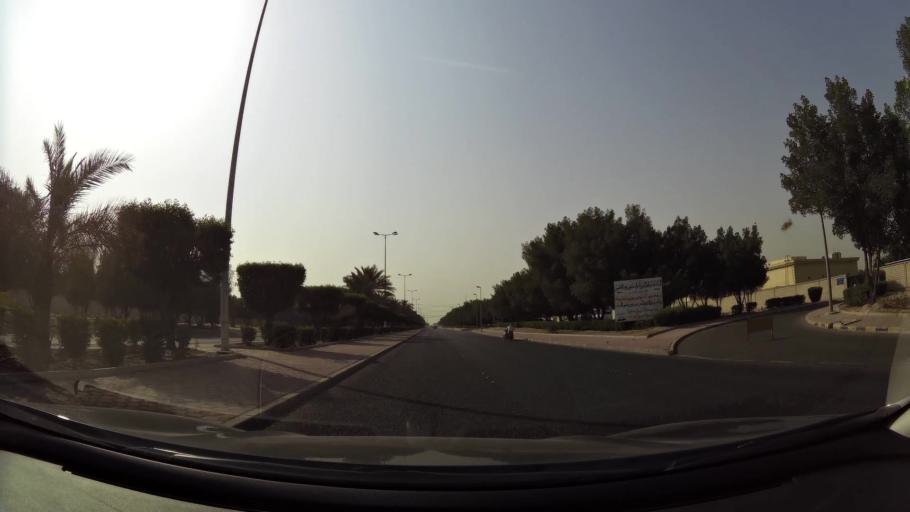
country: KW
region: Al Asimah
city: Ar Rabiyah
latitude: 29.3034
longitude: 47.8321
